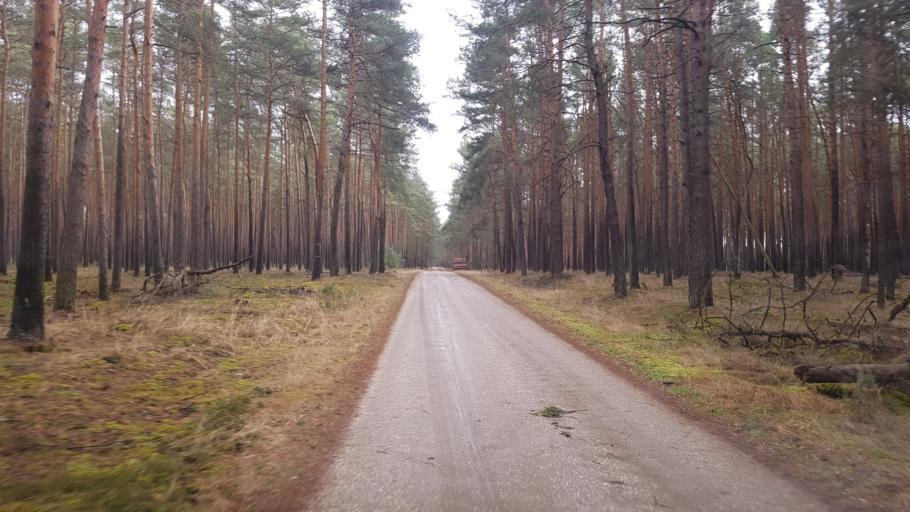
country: DE
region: Brandenburg
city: Sallgast
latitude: 51.6613
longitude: 13.8307
